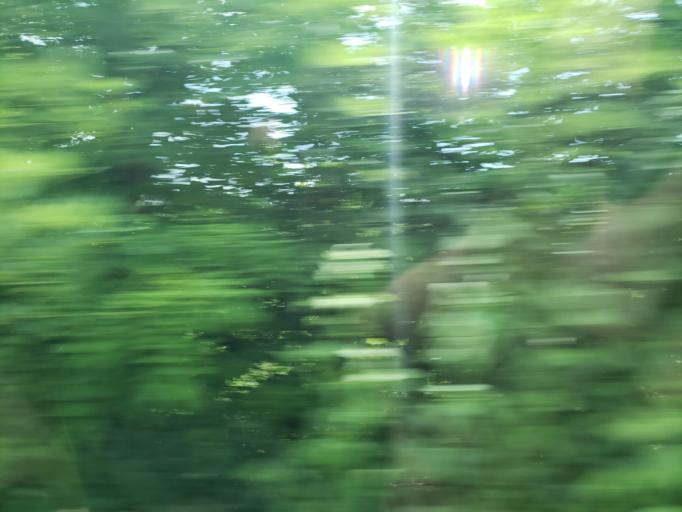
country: ID
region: Bali
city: Kangin
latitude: -8.8423
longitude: 115.1465
